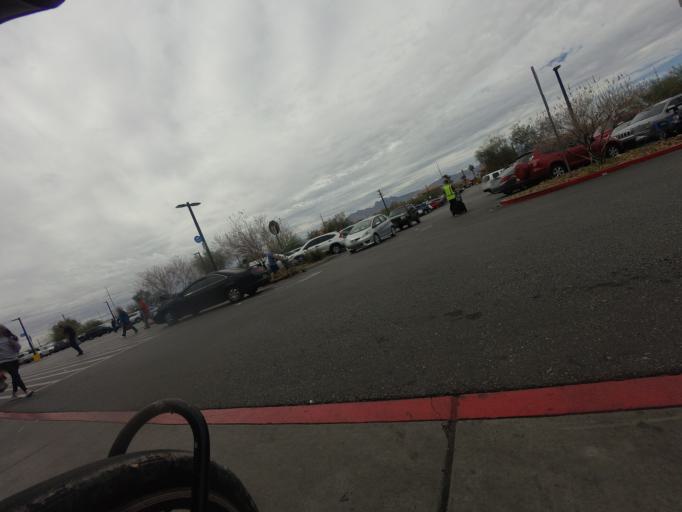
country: US
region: Nevada
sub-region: Clark County
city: North Las Vegas
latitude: 36.2784
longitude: -115.2040
